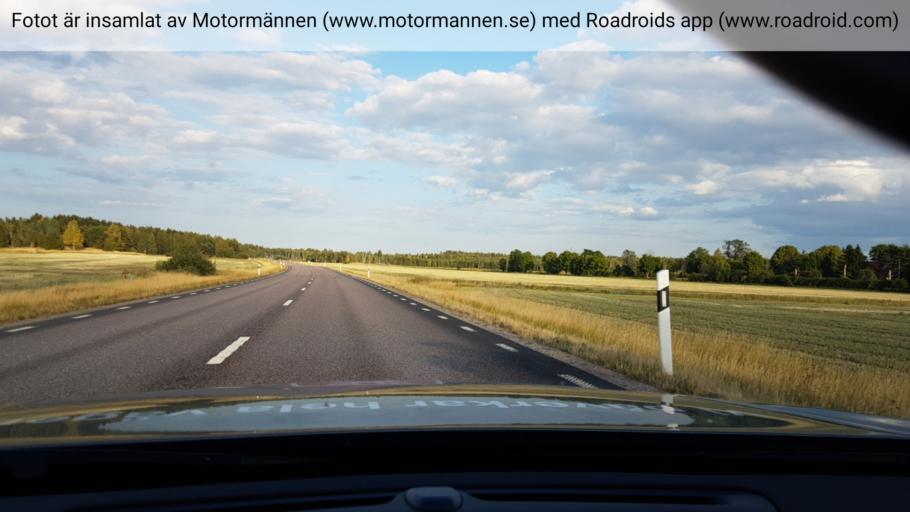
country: SE
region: Uppsala
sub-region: Enkopings Kommun
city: Orsundsbro
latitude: 59.8735
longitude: 17.2967
